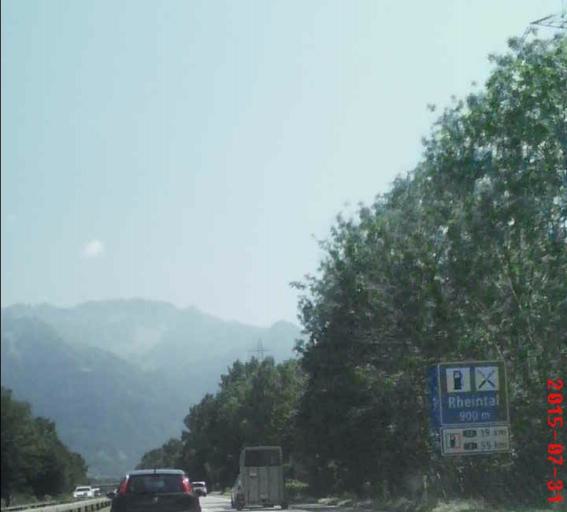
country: CH
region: Saint Gallen
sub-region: Wahlkreis Werdenberg
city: Buchs
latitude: 47.1578
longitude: 9.4922
